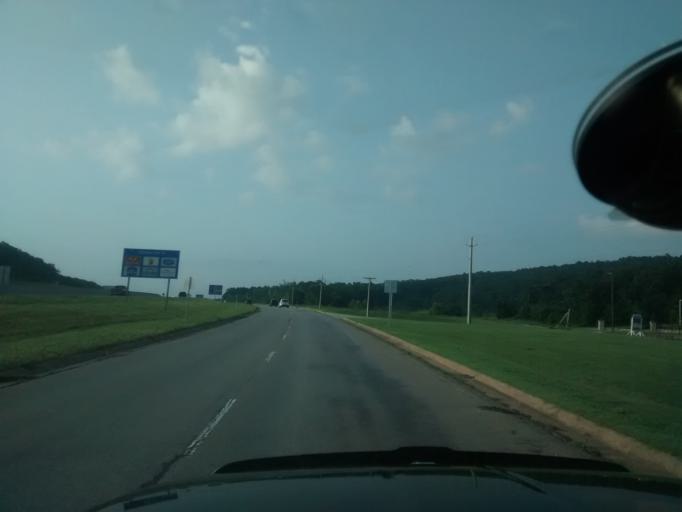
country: US
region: Arkansas
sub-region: Washington County
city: Fayetteville
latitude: 36.0701
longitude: -94.2033
